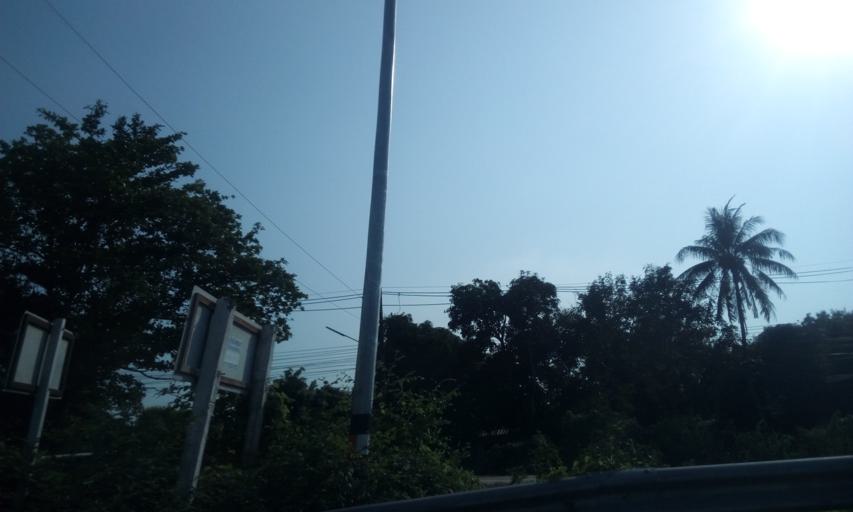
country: TH
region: Sing Buri
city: Sing Buri
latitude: 14.8439
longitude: 100.4251
